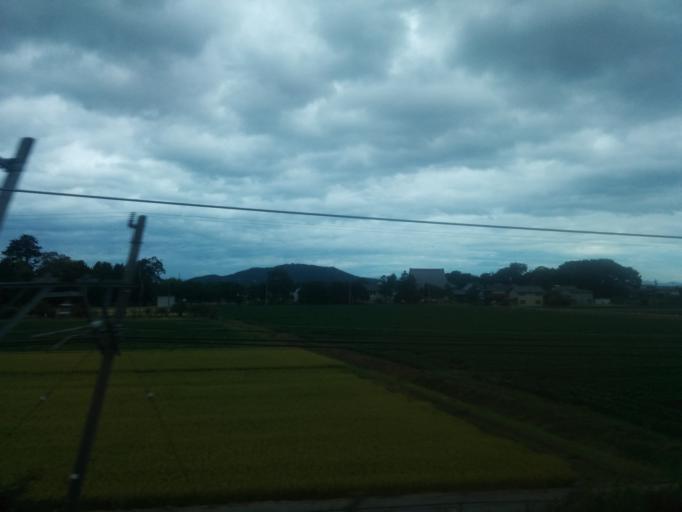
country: JP
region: Shiga Prefecture
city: Hikone
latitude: 35.2042
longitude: 136.2371
